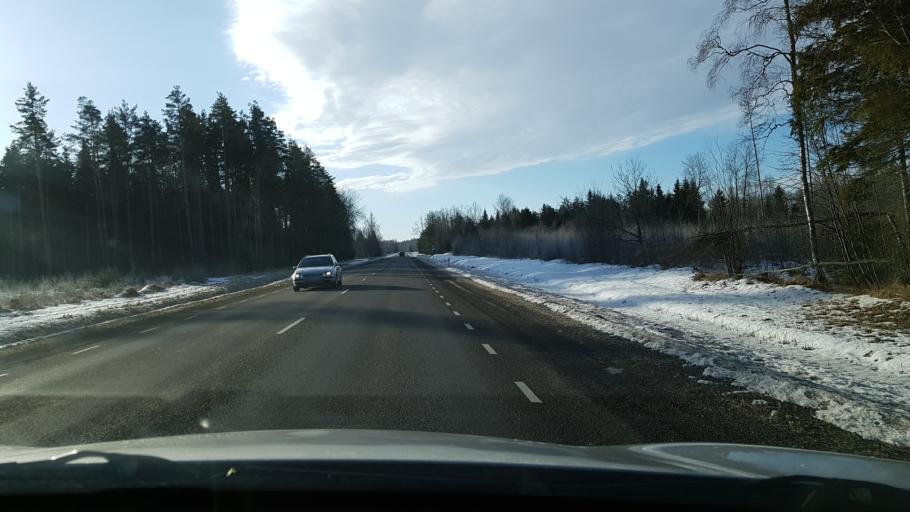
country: EE
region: Viljandimaa
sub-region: Vohma linn
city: Vohma
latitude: 58.5927
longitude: 25.5718
